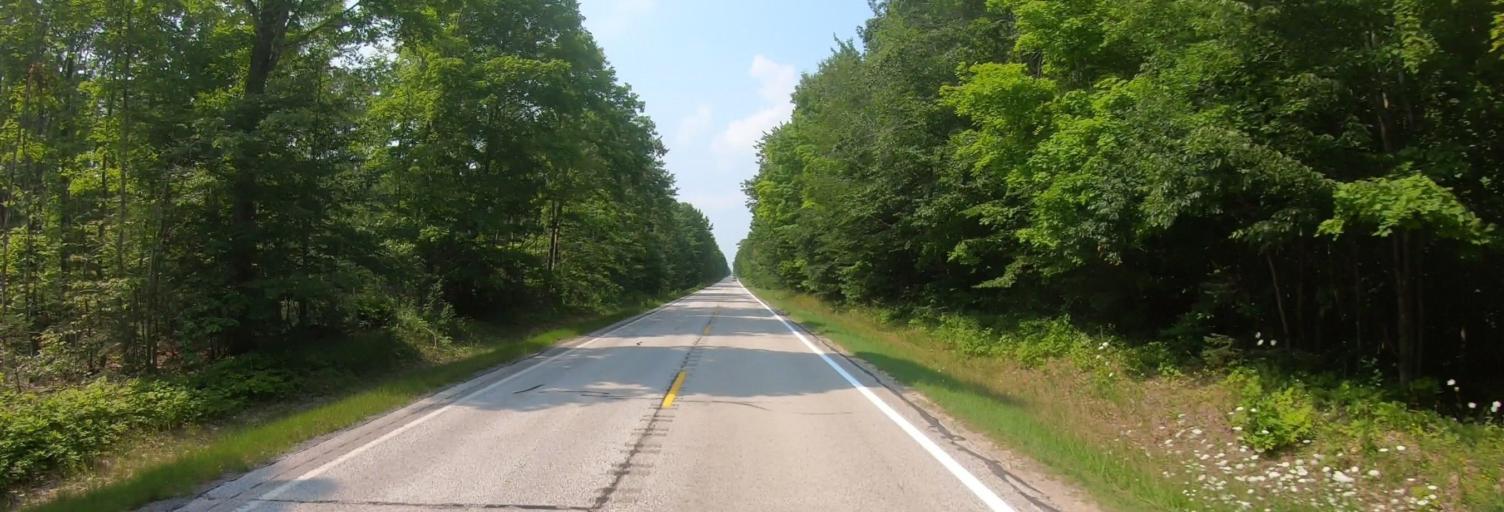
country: US
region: Michigan
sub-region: Luce County
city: Newberry
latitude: 46.5557
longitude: -85.3645
